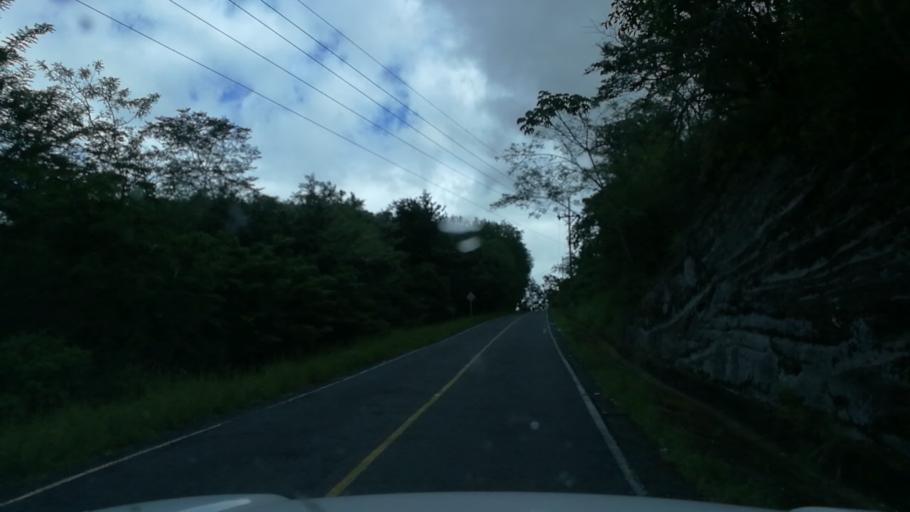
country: CR
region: Guanacaste
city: Fortuna
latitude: 10.6390
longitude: -85.2289
